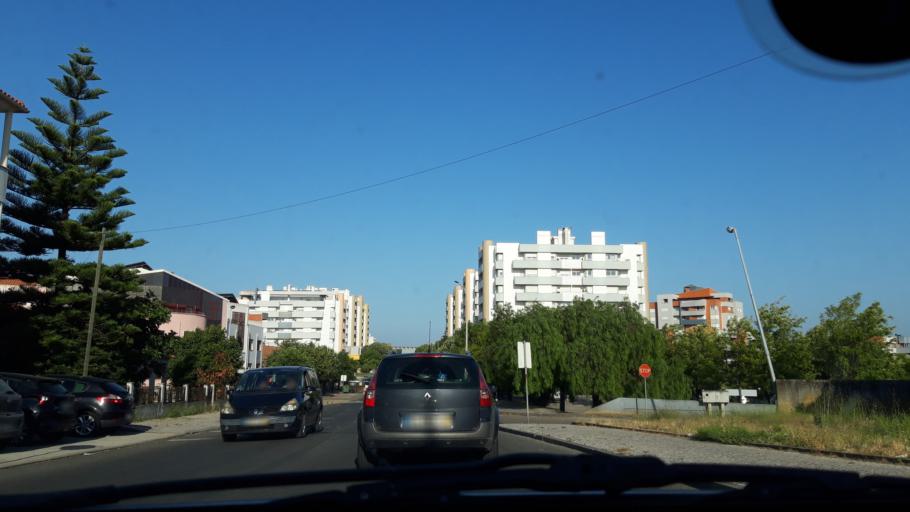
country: PT
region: Santarem
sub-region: Torres Novas
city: Torres Novas
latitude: 39.4740
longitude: -8.5460
